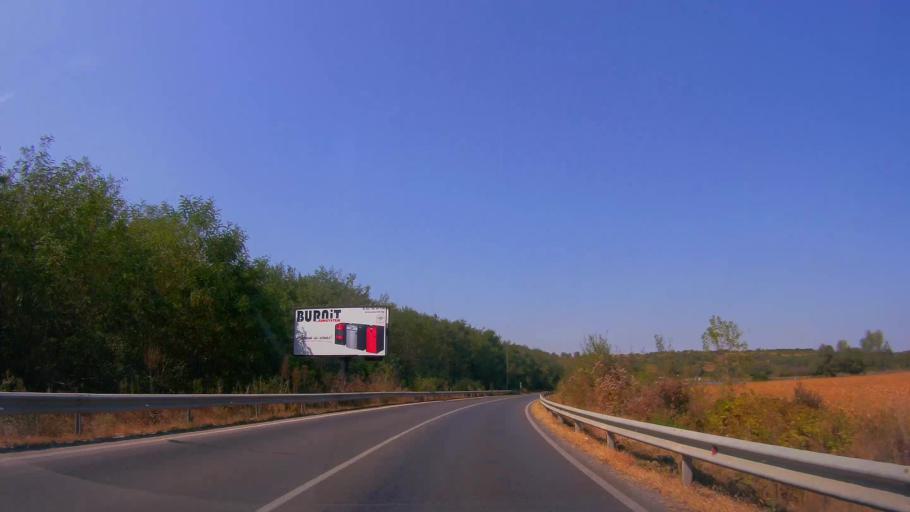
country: BG
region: Razgrad
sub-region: Obshtina Tsar Kaloyan
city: Tsar Kaloyan
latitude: 43.6155
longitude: 26.2151
